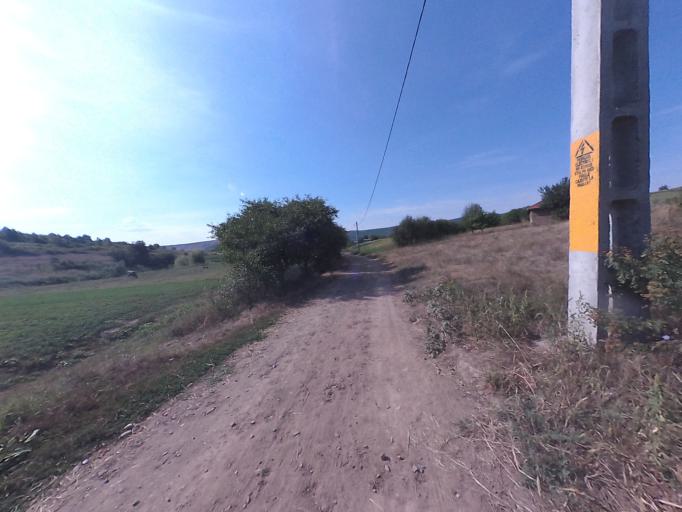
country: RO
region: Vaslui
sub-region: Comuna Osesti
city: Buda
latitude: 46.7679
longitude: 27.4302
